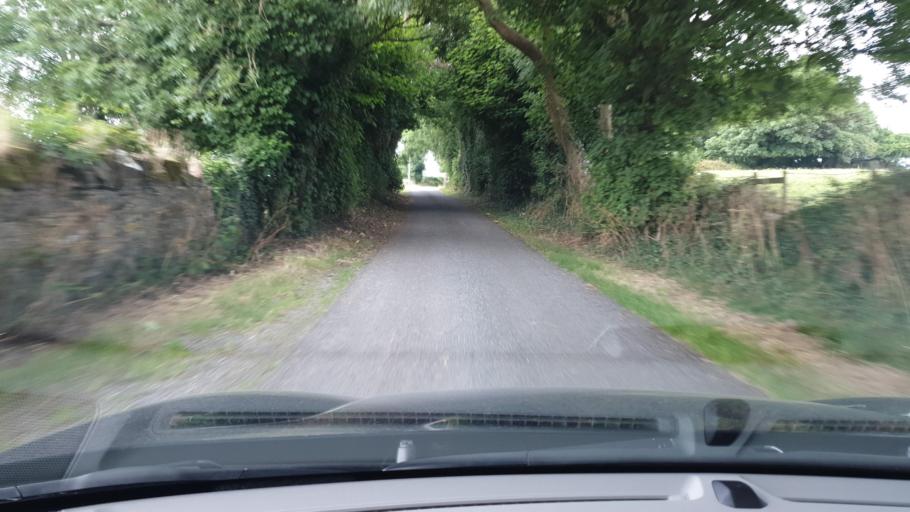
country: IE
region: Leinster
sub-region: An Mhi
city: Ashbourne
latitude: 53.5534
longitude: -6.3875
